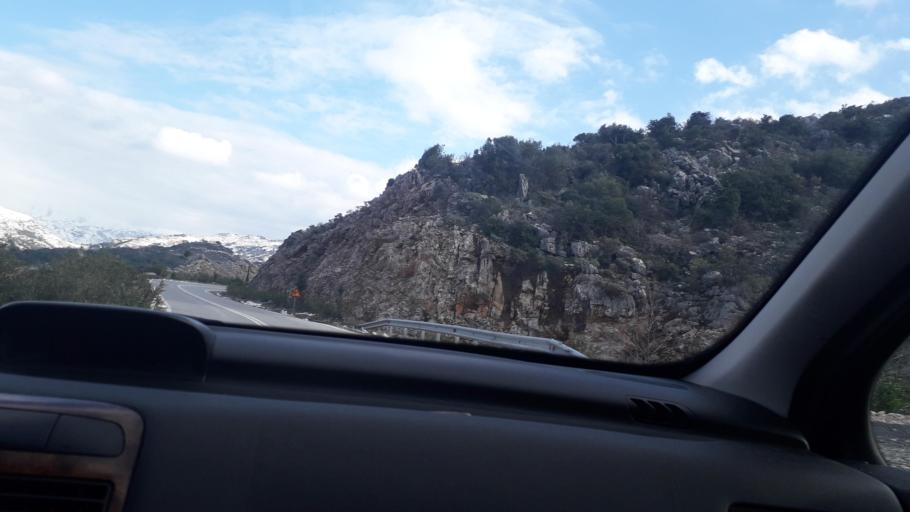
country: GR
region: Crete
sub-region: Nomos Rethymnis
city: Agia Foteini
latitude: 35.2616
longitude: 24.5623
